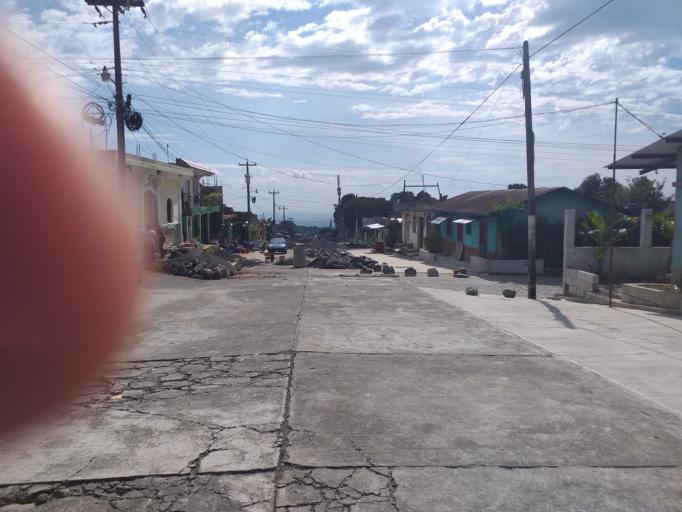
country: GT
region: Suchitepeque
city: Pueblo Nuevo
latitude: 14.6481
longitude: -91.5541
